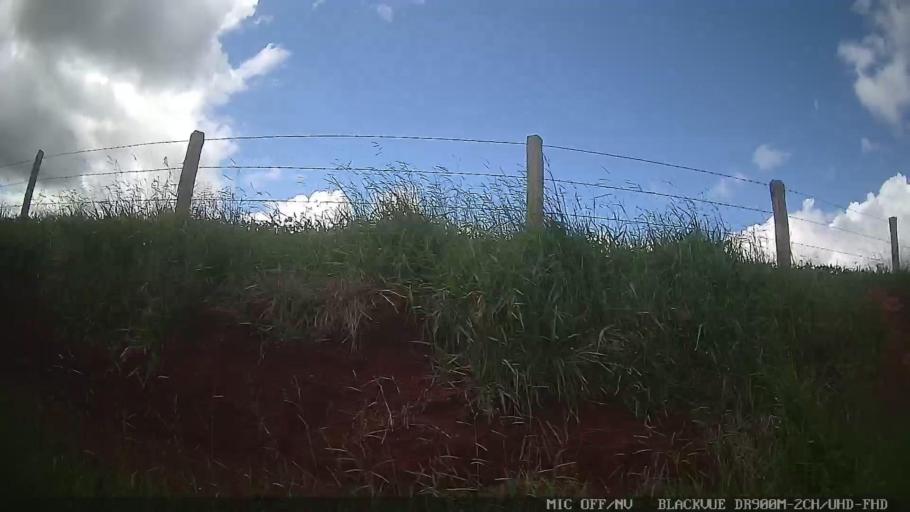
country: BR
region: Sao Paulo
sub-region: Braganca Paulista
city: Braganca Paulista
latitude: -22.8626
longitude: -46.6470
